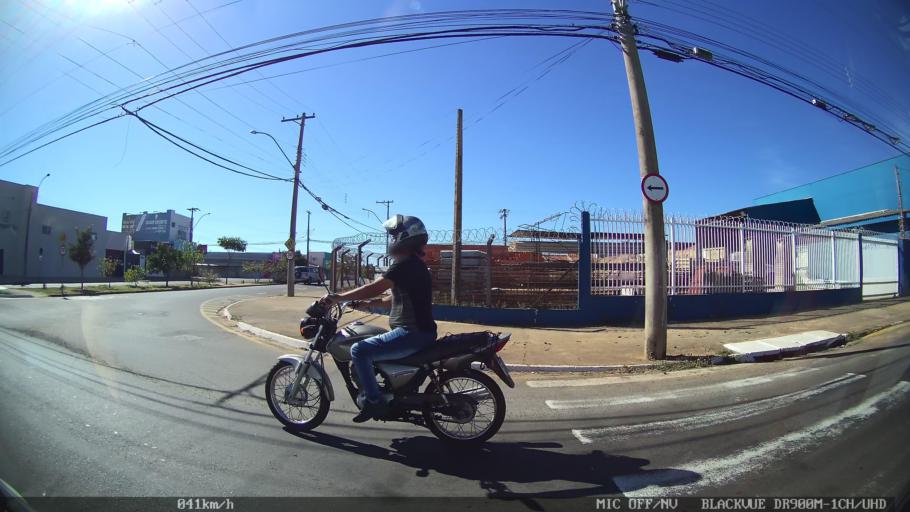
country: BR
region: Sao Paulo
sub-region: Franca
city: Franca
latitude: -20.5506
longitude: -47.3602
